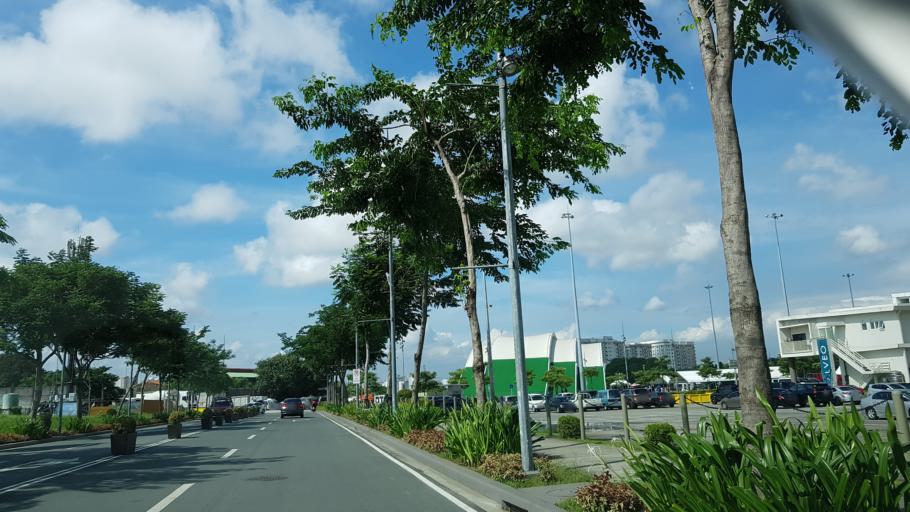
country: PH
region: Metro Manila
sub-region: Mandaluyong
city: Mandaluyong City
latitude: 14.5757
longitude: 121.0186
